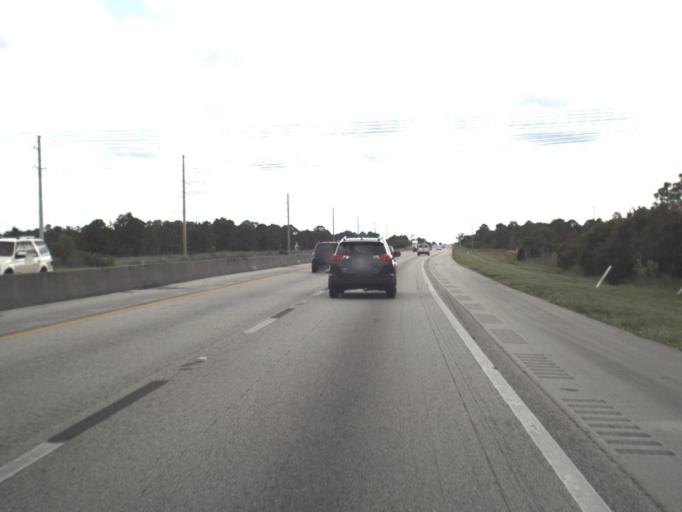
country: US
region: Florida
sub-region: Saint Lucie County
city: River Park
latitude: 27.3515
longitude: -80.3744
